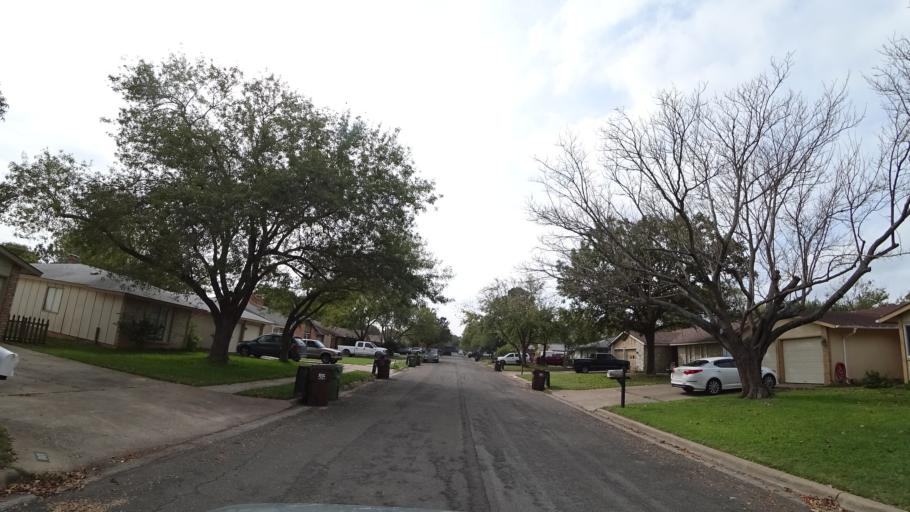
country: US
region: Texas
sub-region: Williamson County
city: Round Rock
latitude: 30.4947
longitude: -97.6882
